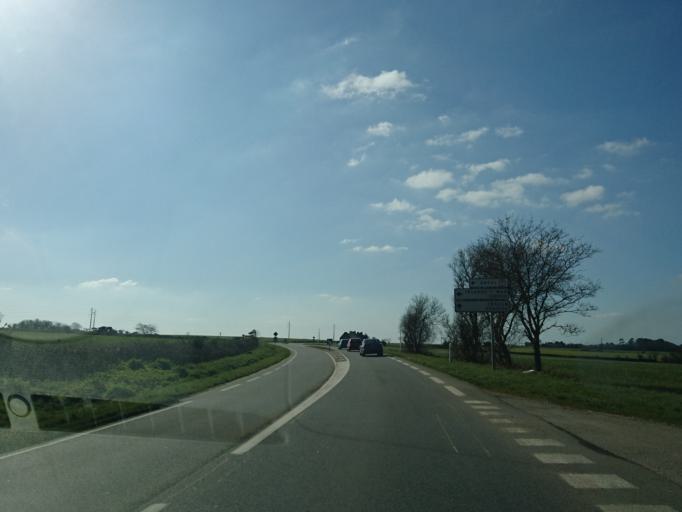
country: FR
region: Brittany
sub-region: Departement du Finistere
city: Telgruc-sur-Mer
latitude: 48.2652
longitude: -4.3036
